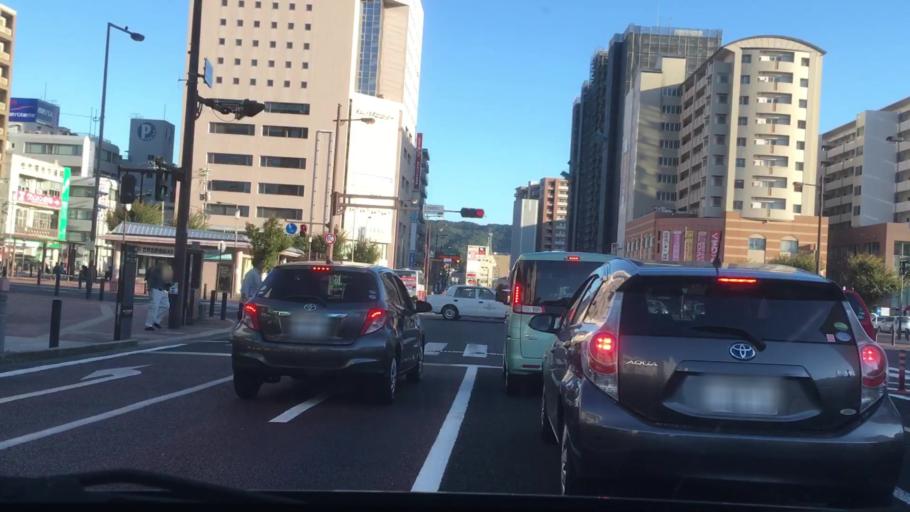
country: JP
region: Nagasaki
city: Sasebo
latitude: 33.1649
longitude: 129.7264
